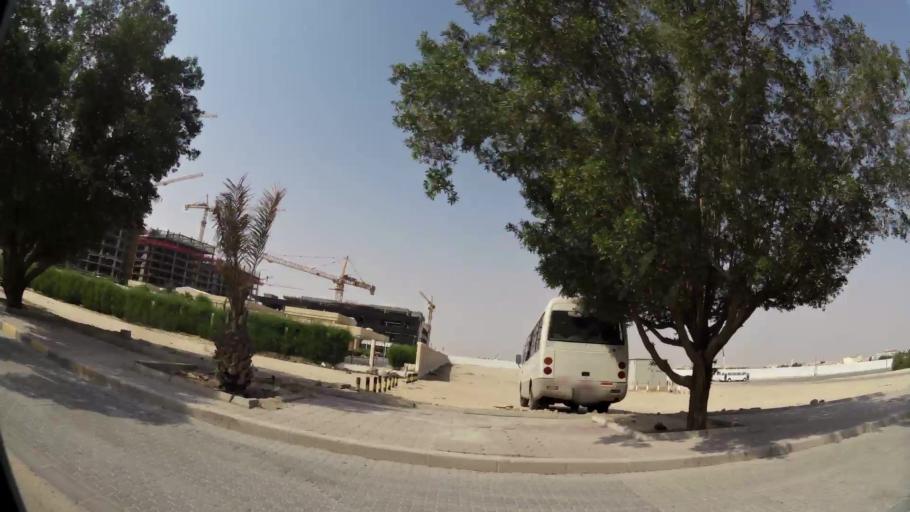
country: KW
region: Muhafazat al Jahra'
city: Al Jahra'
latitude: 29.3380
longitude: 47.6862
